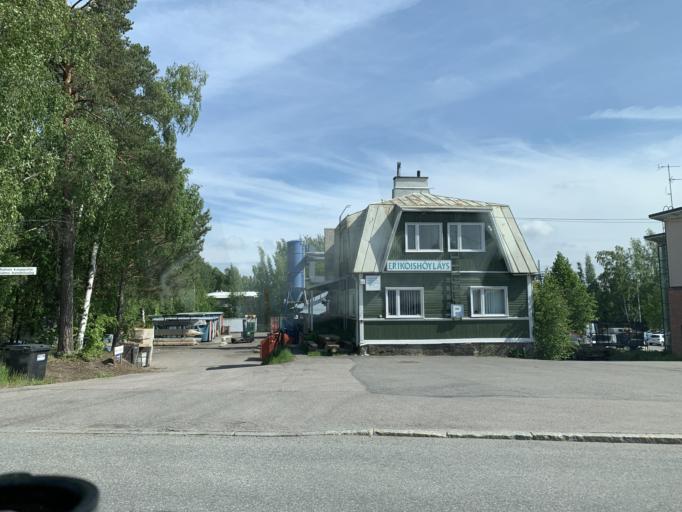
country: FI
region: Uusimaa
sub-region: Helsinki
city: Vantaa
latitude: 60.2600
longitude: 25.0222
